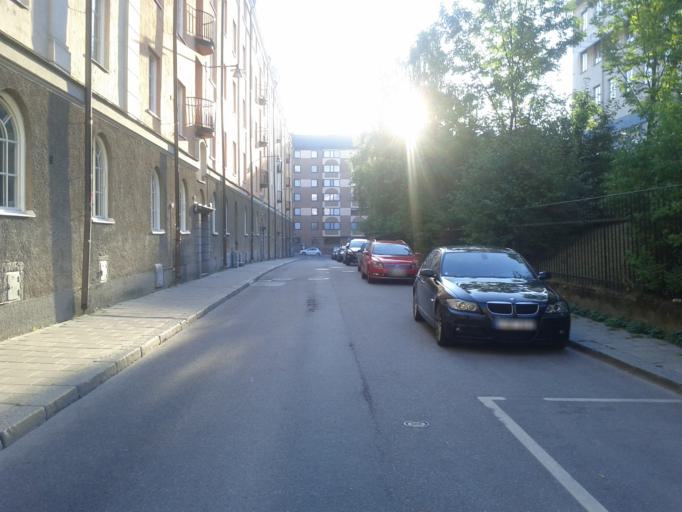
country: SE
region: Stockholm
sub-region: Stockholms Kommun
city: Stockholm
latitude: 59.3344
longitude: 18.0378
